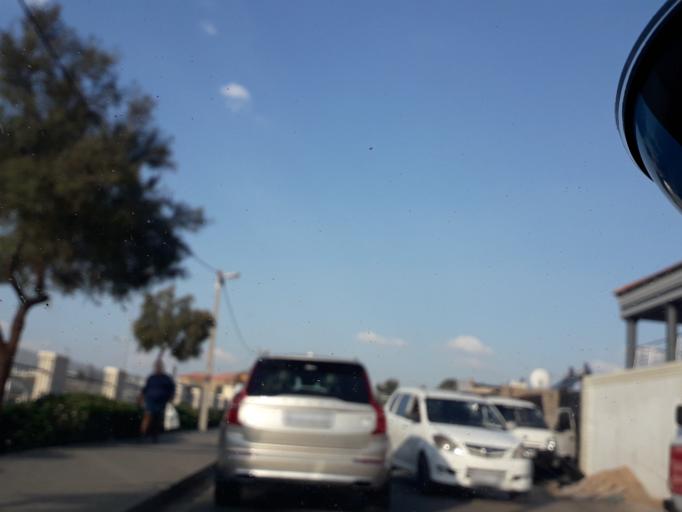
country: ZA
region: Gauteng
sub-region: City of Johannesburg Metropolitan Municipality
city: Modderfontein
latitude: -26.0845
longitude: 28.1115
